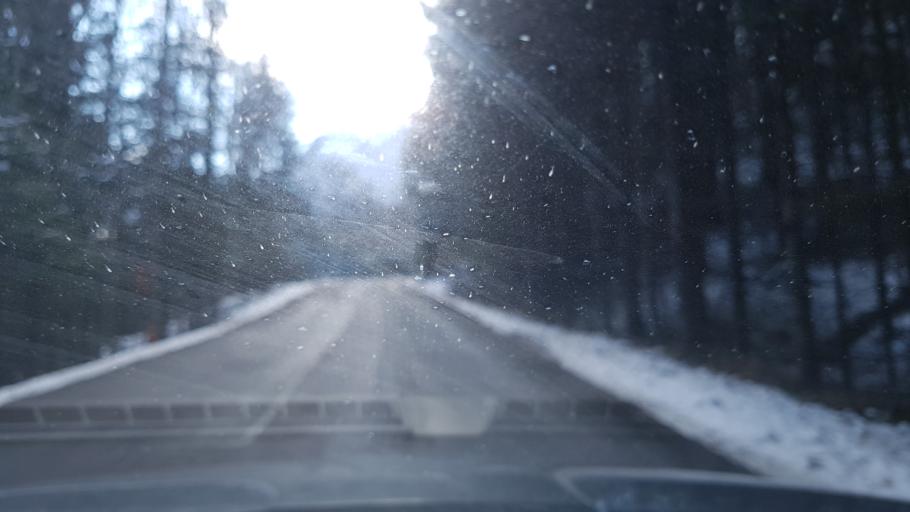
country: AT
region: Salzburg
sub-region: Politischer Bezirk Hallein
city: Kuchl
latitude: 47.6150
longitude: 13.1355
